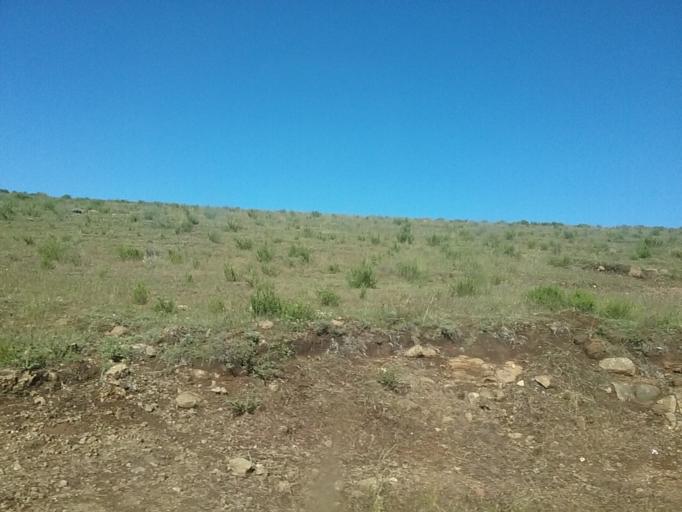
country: LS
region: Berea
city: Teyateyaneng
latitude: -29.2363
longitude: 27.9078
